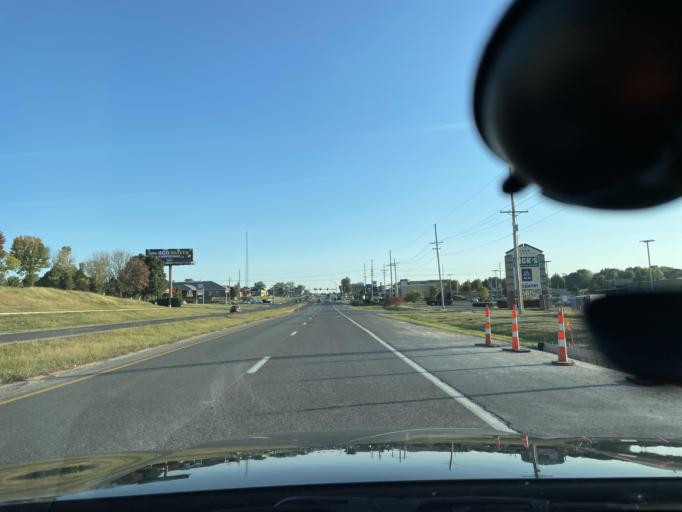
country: US
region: Missouri
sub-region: Andrew County
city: Country Club Village
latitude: 39.8090
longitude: -94.8153
